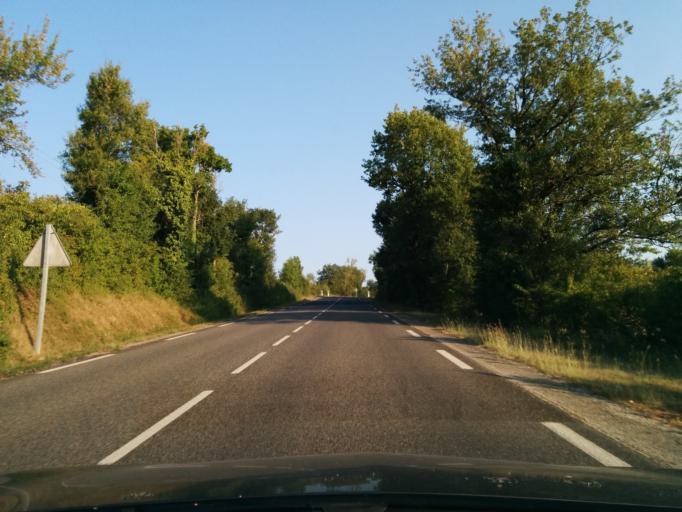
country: FR
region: Midi-Pyrenees
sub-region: Departement du Lot
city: Le Vigan
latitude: 44.6445
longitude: 1.4801
